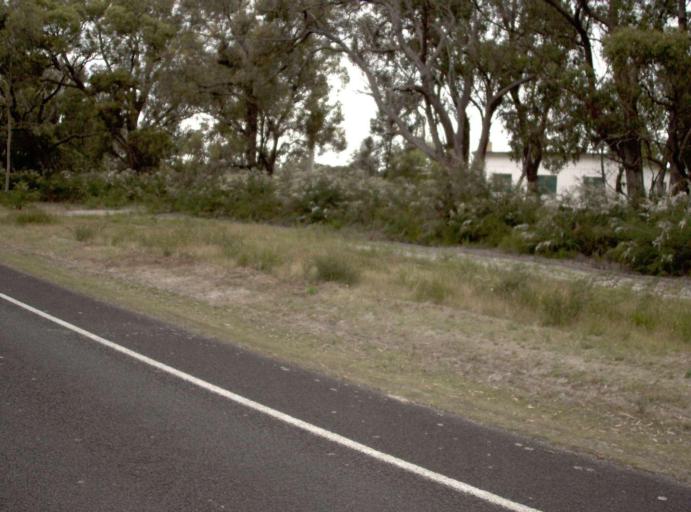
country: AU
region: Victoria
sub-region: Wellington
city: Sale
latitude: -38.3447
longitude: 147.0027
